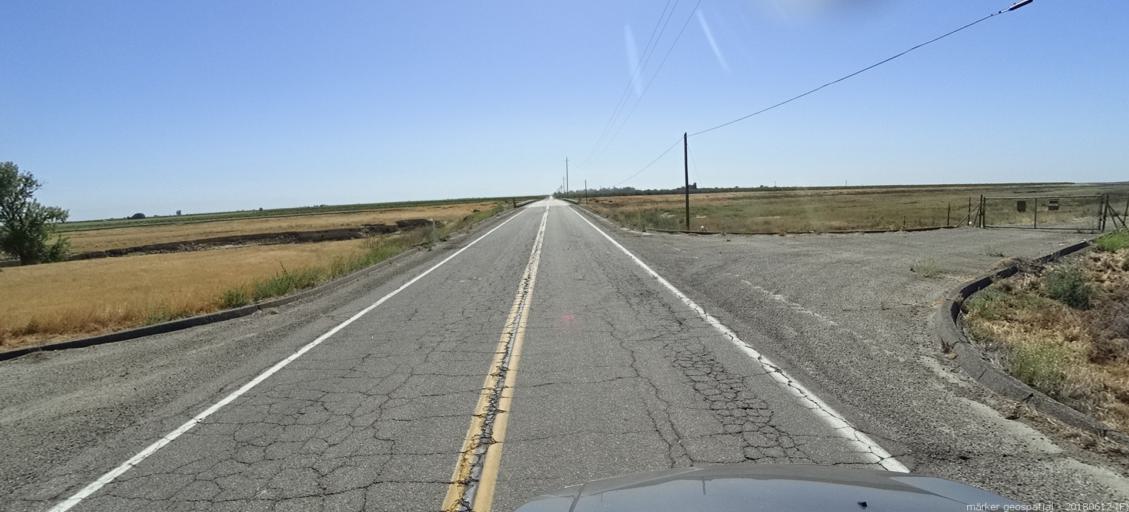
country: US
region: California
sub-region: Fresno County
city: Firebaugh
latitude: 37.0182
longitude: -120.4353
